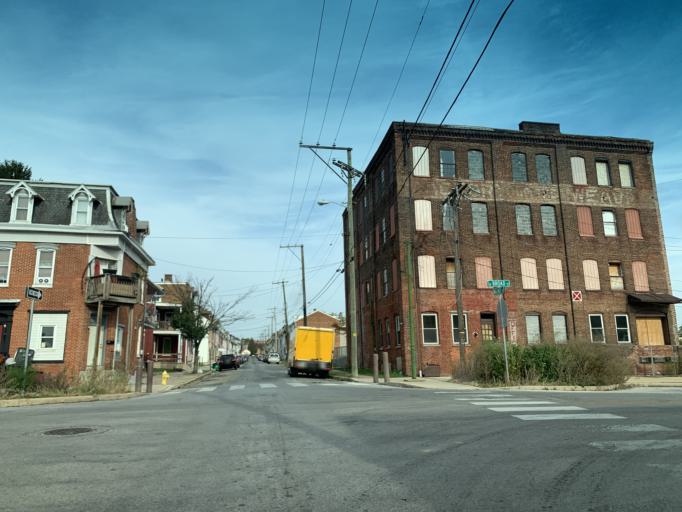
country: US
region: Pennsylvania
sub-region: York County
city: York
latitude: 39.9674
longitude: -76.7206
